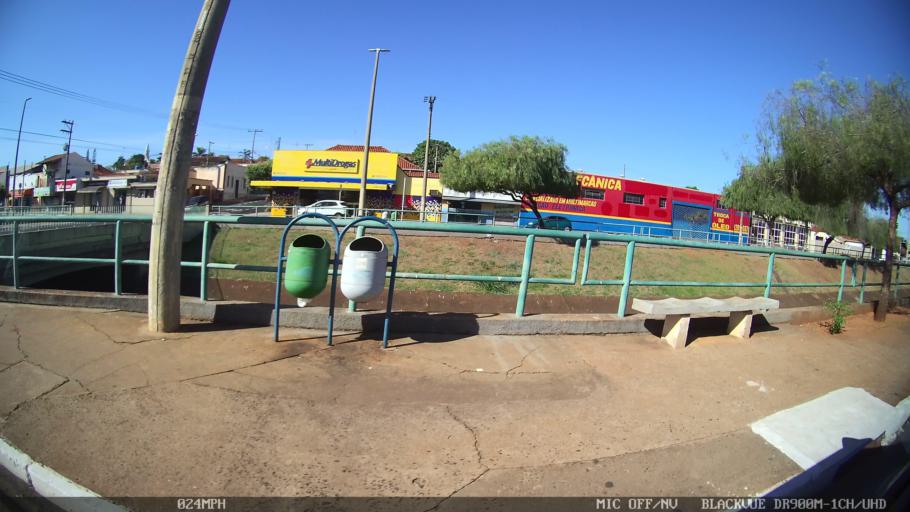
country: BR
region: Sao Paulo
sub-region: Olimpia
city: Olimpia
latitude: -20.7394
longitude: -48.9104
